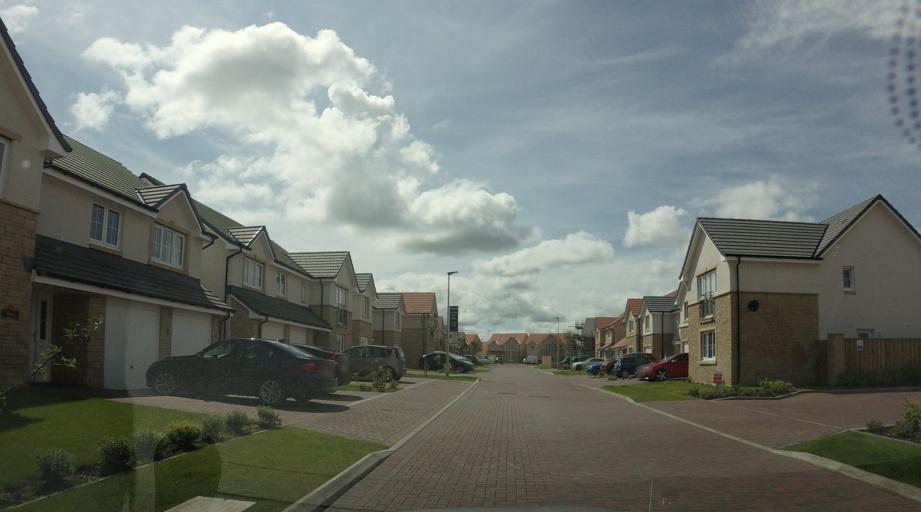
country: GB
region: Scotland
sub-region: West Lothian
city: Broxburn
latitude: 55.9326
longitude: -3.4610
